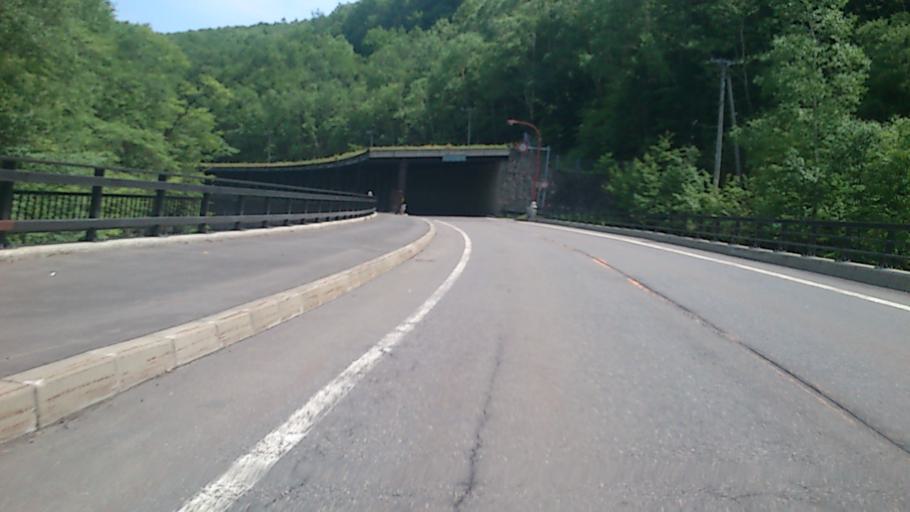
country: JP
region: Hokkaido
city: Otofuke
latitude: 43.3623
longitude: 143.2362
